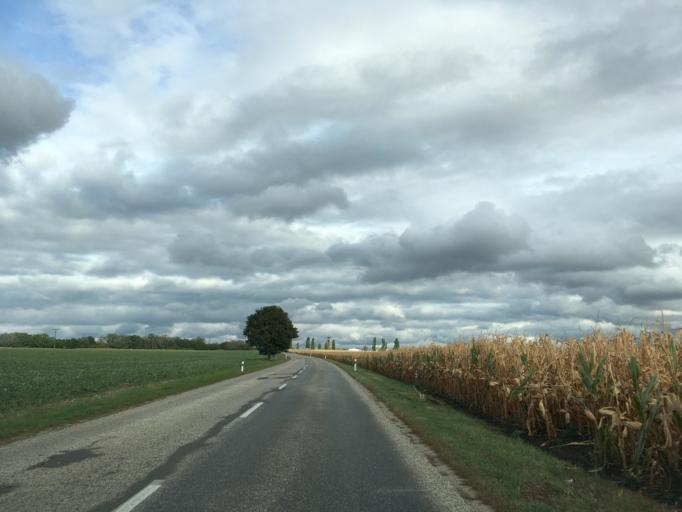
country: SK
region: Nitriansky
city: Svodin
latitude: 47.9826
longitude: 18.3759
